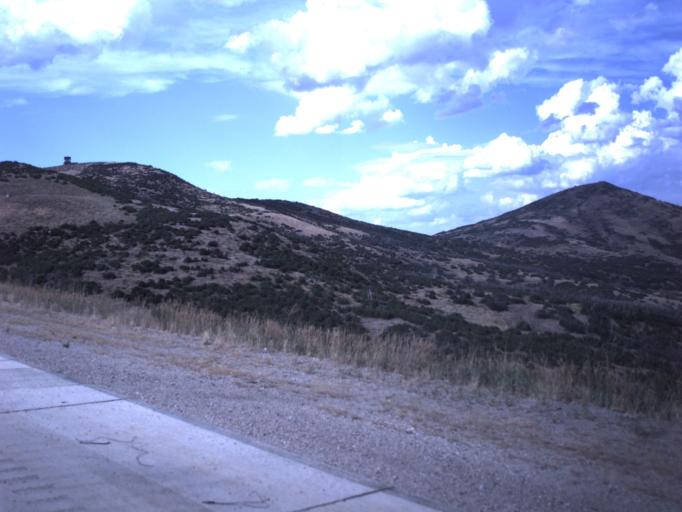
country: US
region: Utah
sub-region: Summit County
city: Park City
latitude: 40.6432
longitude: -111.4532
